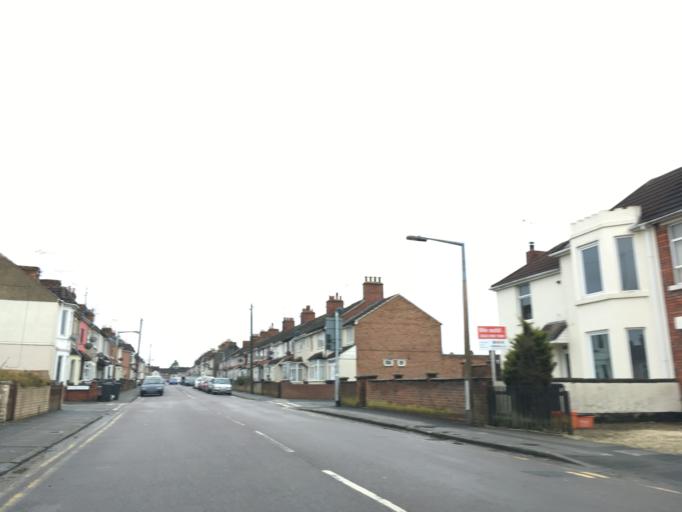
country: GB
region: England
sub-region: Borough of Swindon
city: Swindon
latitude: 51.5659
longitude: -1.8047
